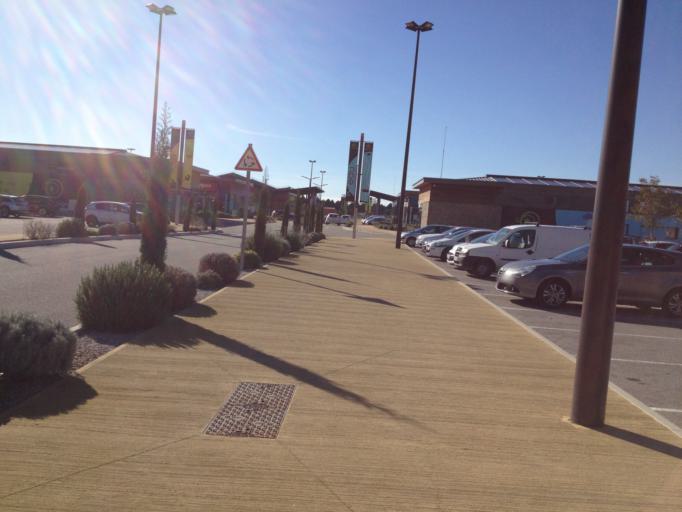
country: FR
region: Provence-Alpes-Cote d'Azur
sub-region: Departement du Vaucluse
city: Courthezon
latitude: 44.1109
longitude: 4.8530
